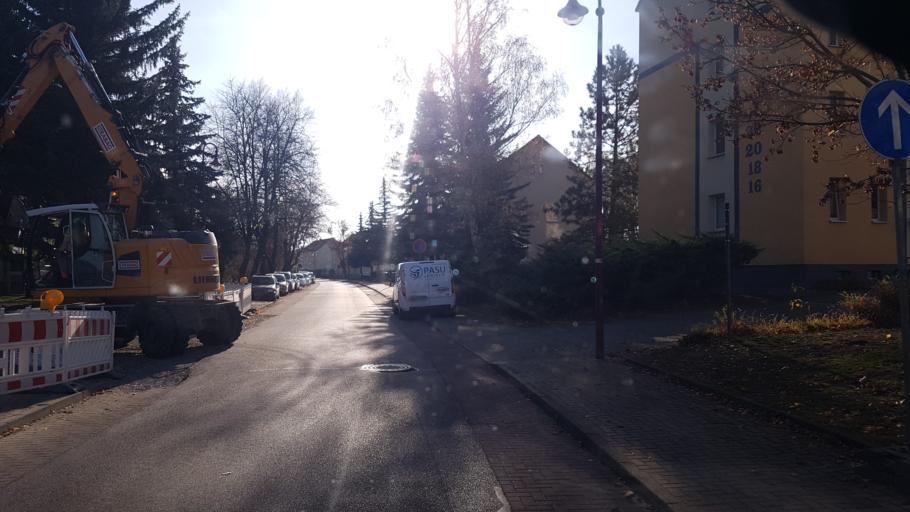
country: DE
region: Brandenburg
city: Grossraschen
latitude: 51.5888
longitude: 13.9970
